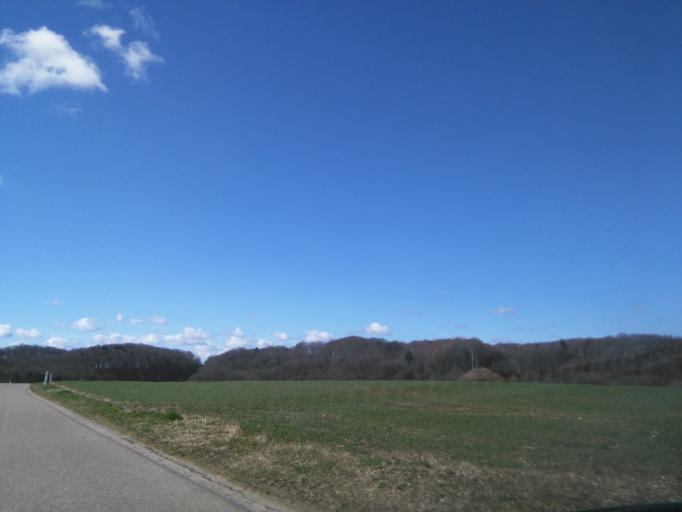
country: DK
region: Central Jutland
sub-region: Skanderborg Kommune
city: Stilling
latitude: 56.0953
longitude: 9.9882
